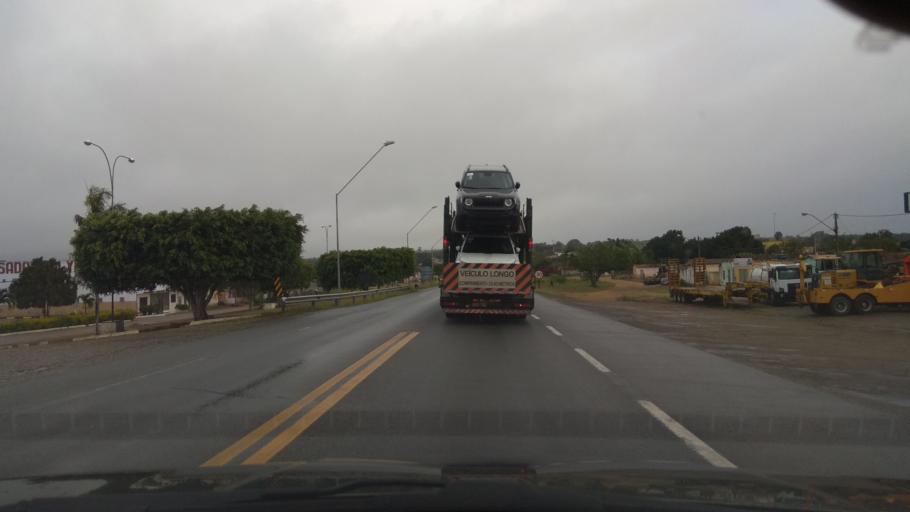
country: BR
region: Bahia
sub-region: Santa Ines
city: Santa Ines
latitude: -13.0754
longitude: -39.9615
